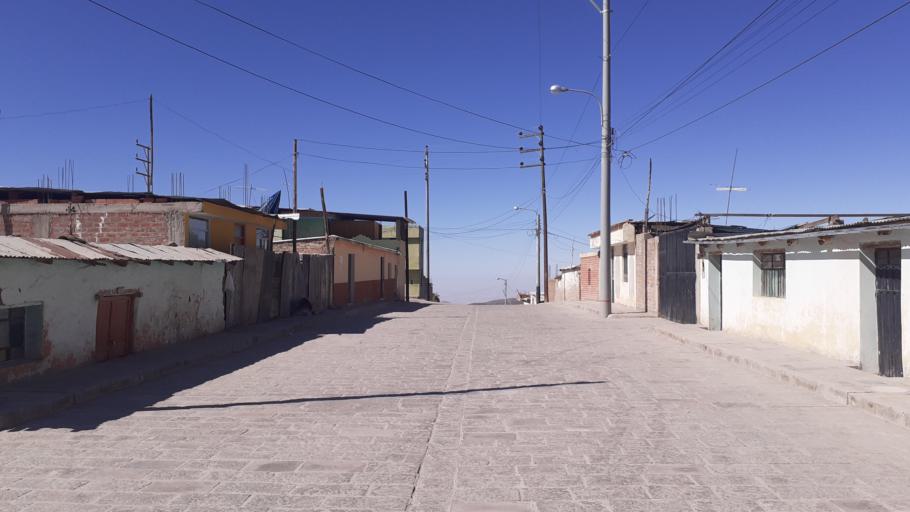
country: PE
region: Arequipa
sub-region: Provincia de Condesuyos
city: Chuquibamba
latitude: -15.8385
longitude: -72.6557
